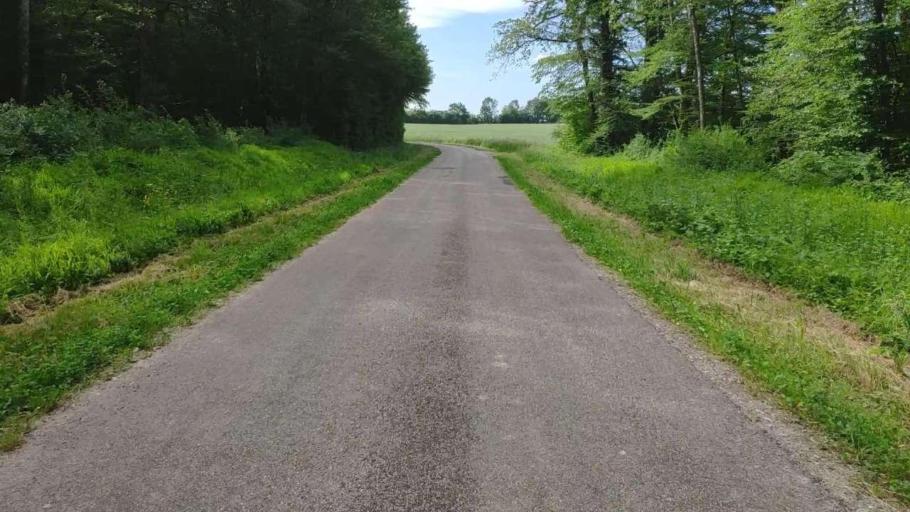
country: FR
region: Franche-Comte
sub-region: Departement du Jura
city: Bletterans
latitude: 46.6901
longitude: 5.4241
